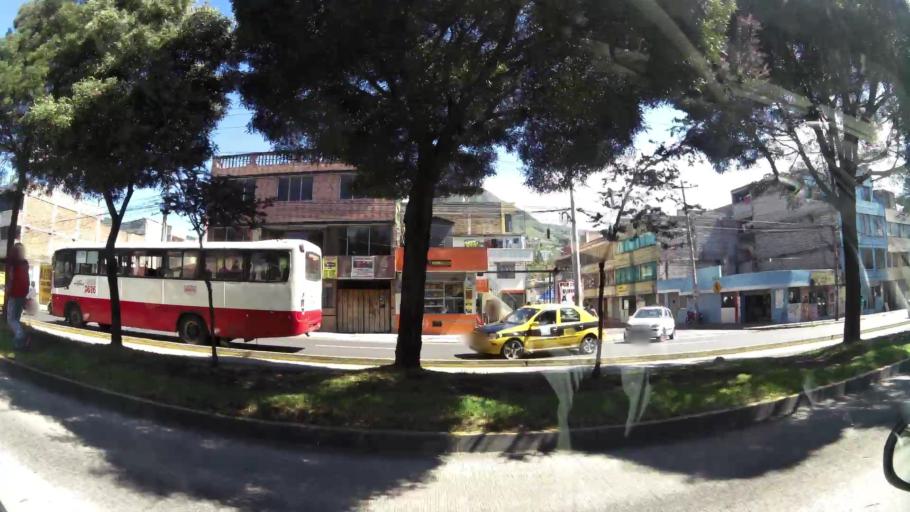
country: EC
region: Pichincha
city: Quito
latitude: -0.2559
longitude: -78.5420
